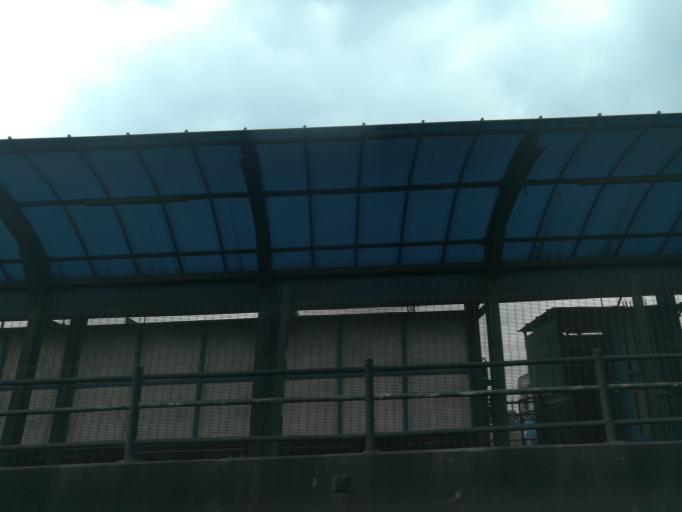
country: NG
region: Lagos
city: Ojota
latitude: 6.6079
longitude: 3.4085
